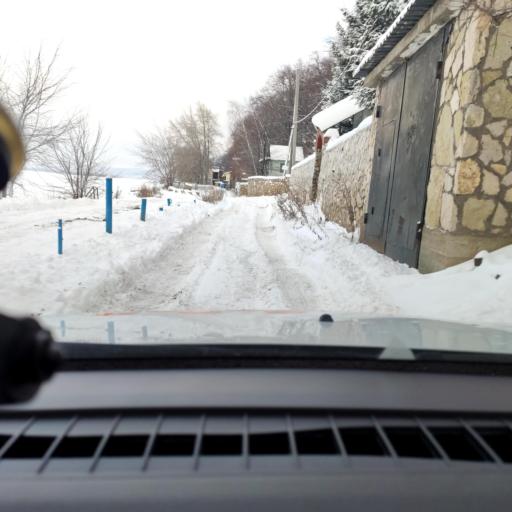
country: RU
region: Samara
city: Samara
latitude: 53.2891
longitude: 50.1917
